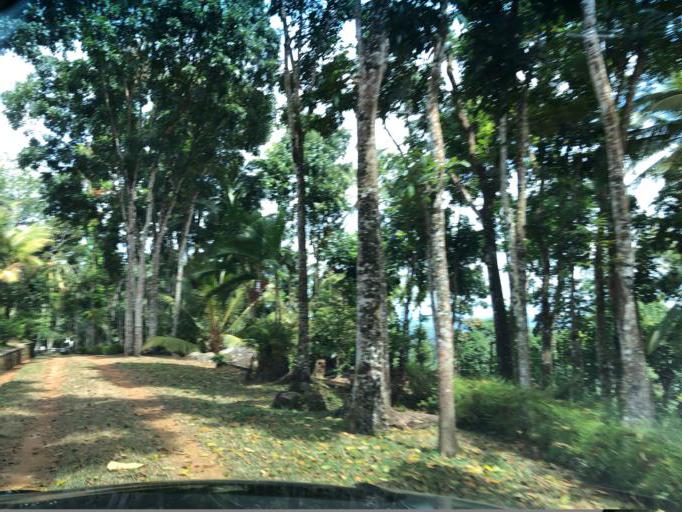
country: LK
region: Western
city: Horawala Junction
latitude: 6.5494
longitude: 80.0870
